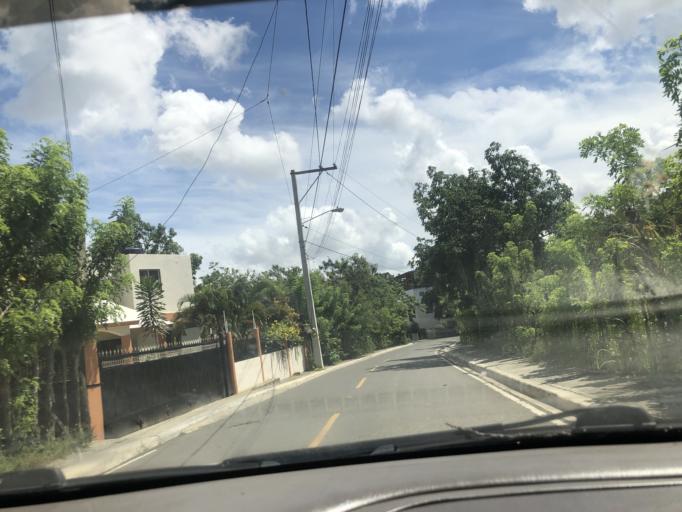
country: DO
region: Santiago
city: Santiago de los Caballeros
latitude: 19.4135
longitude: -70.7054
